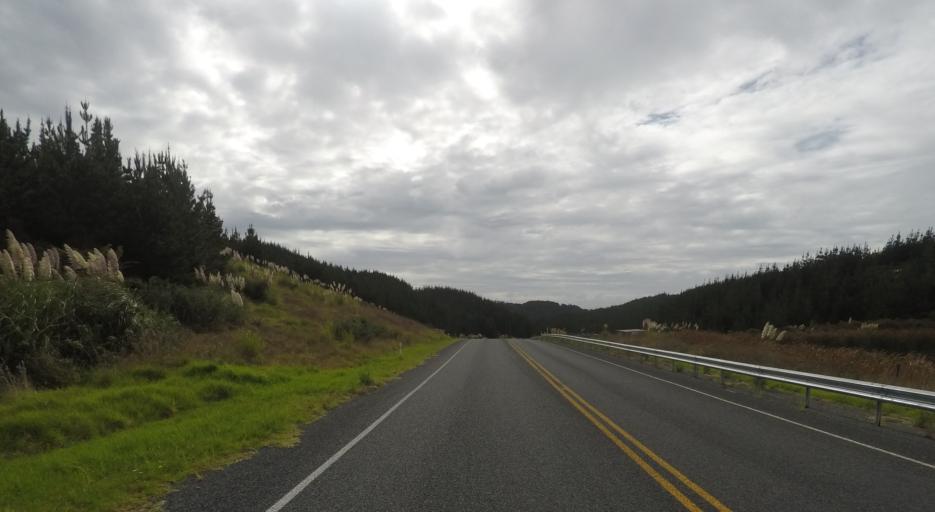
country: NZ
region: Auckland
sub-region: Auckland
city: Rothesay Bay
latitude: -36.6549
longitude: 174.7001
